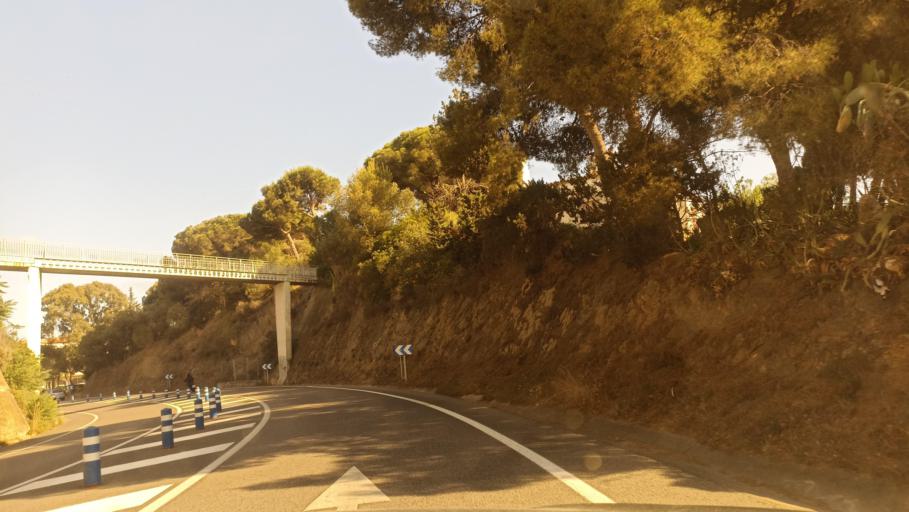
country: ES
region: Catalonia
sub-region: Provincia de Barcelona
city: Sant Pol de Mar
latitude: 41.6031
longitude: 2.6258
